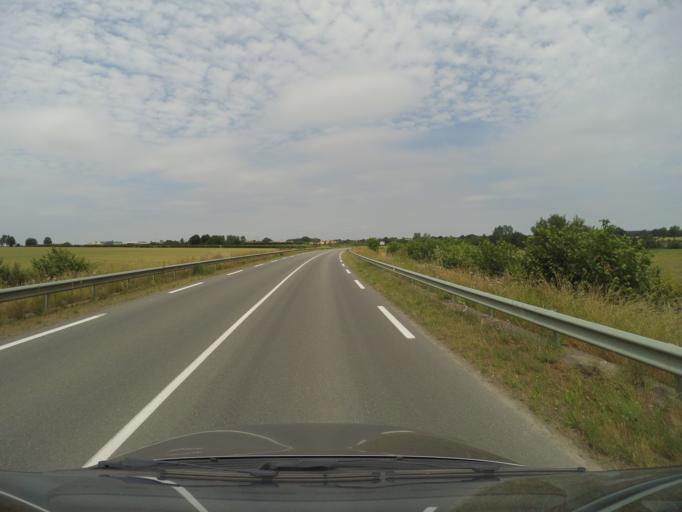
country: FR
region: Pays de la Loire
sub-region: Departement de la Vendee
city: Les Herbiers
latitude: 46.8489
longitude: -1.0535
